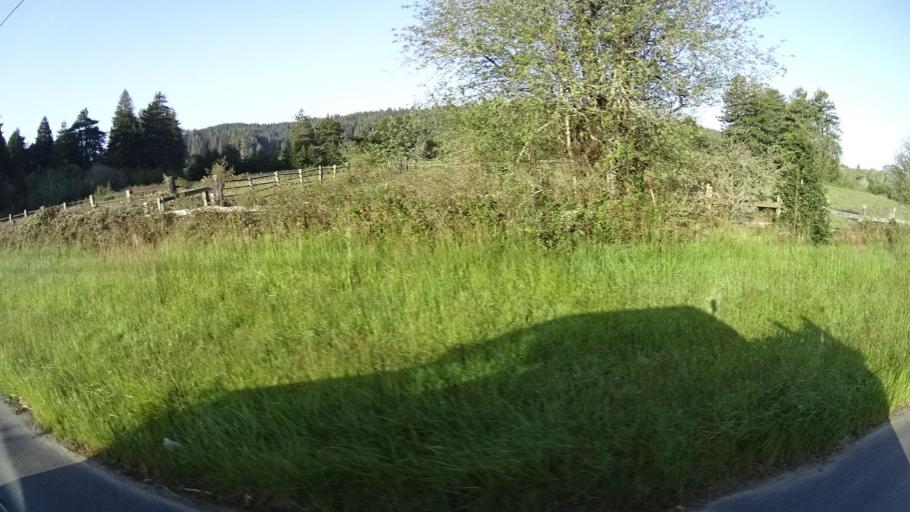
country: US
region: California
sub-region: Humboldt County
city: Myrtletown
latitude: 40.7794
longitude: -124.0756
